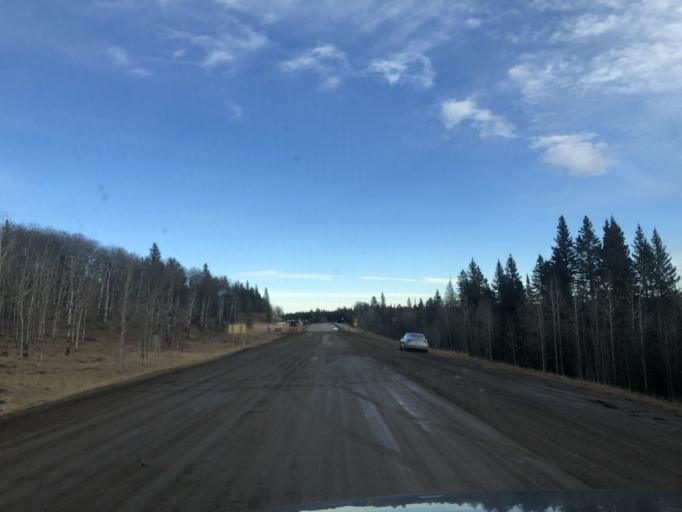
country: CA
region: Alberta
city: Cochrane
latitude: 51.0372
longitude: -114.7275
